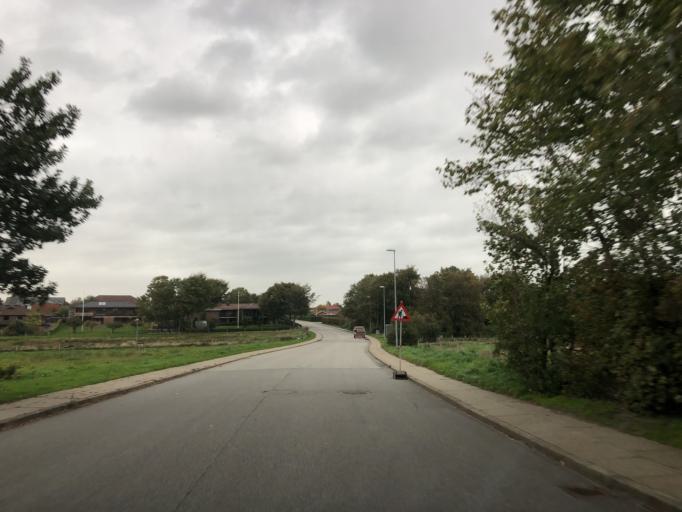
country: DK
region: Central Jutland
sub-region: Herning Kommune
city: Avlum
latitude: 56.2680
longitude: 8.7944
